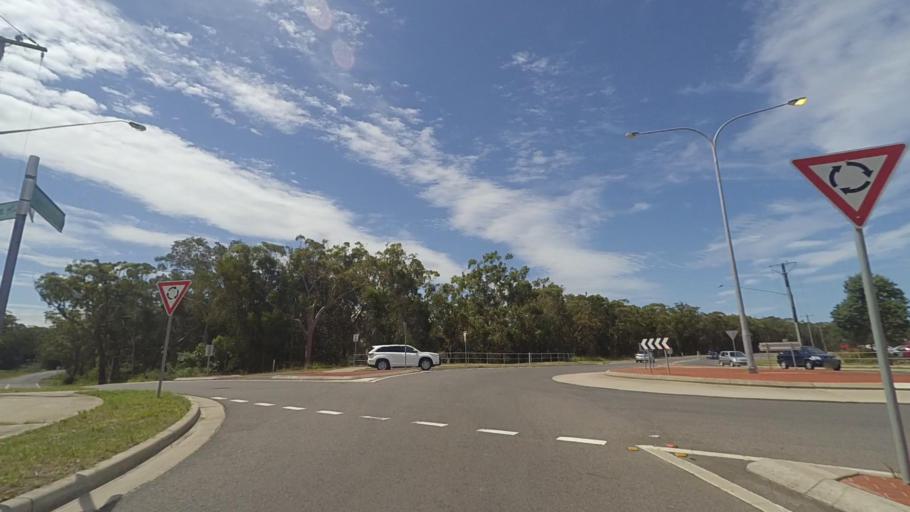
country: AU
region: New South Wales
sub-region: Port Stephens Shire
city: Anna Bay
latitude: -32.7495
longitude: 152.0685
